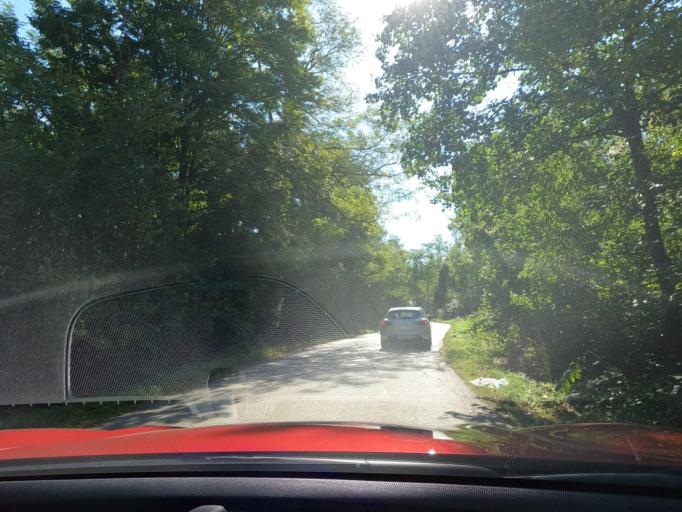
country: RS
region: Central Serbia
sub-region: Raski Okrug
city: Kraljevo
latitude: 43.7710
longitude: 20.6602
